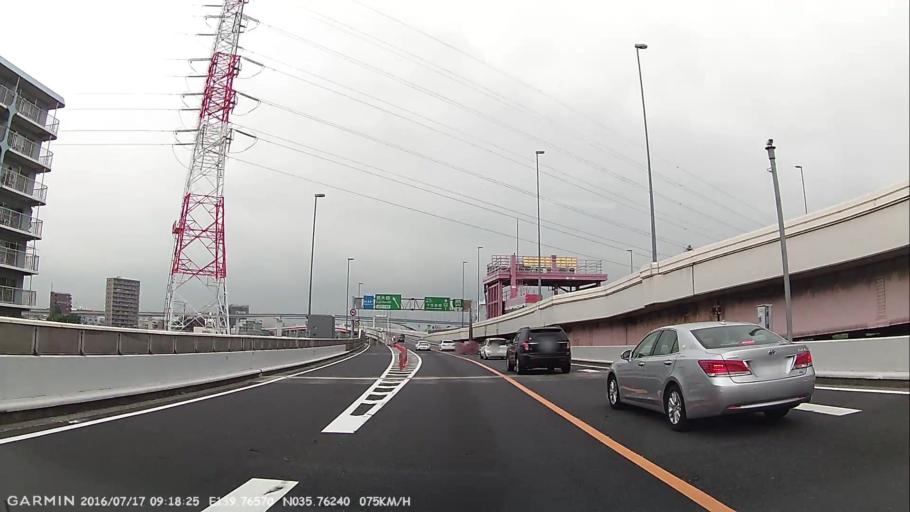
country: JP
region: Saitama
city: Soka
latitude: 35.7624
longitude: 139.7659
